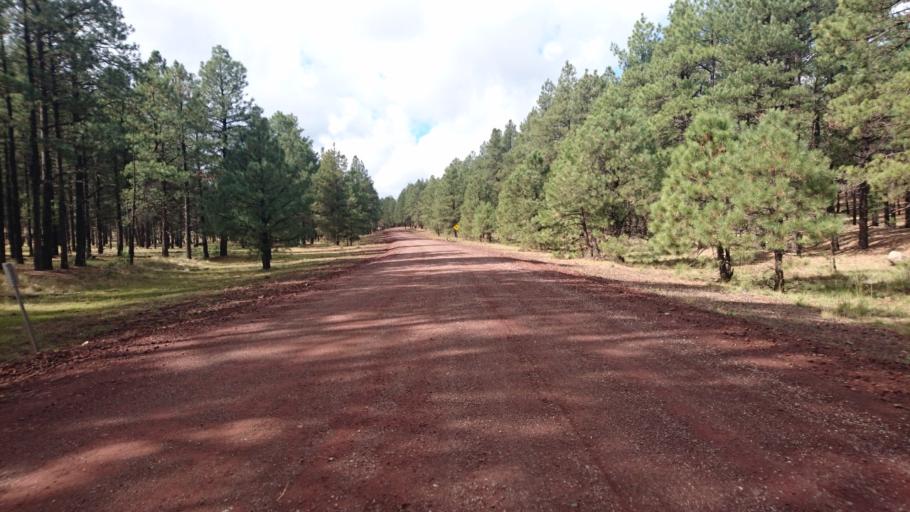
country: US
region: Arizona
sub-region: Coconino County
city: Parks
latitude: 35.2754
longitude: -111.9003
